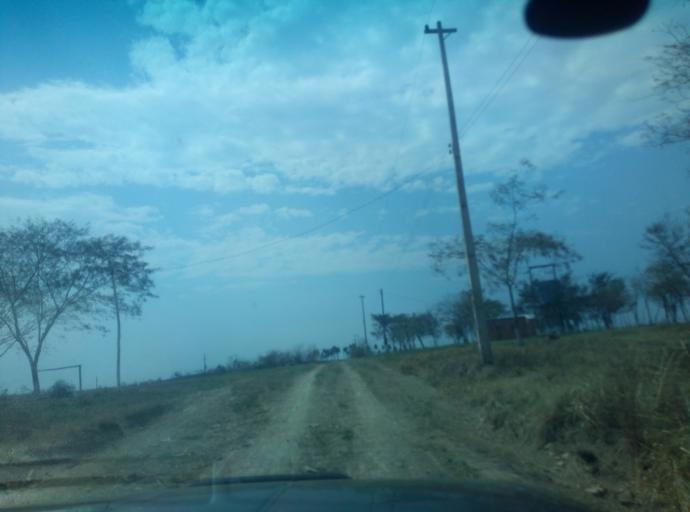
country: PY
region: Caaguazu
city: Doctor Cecilio Baez
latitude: -25.1380
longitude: -56.1596
